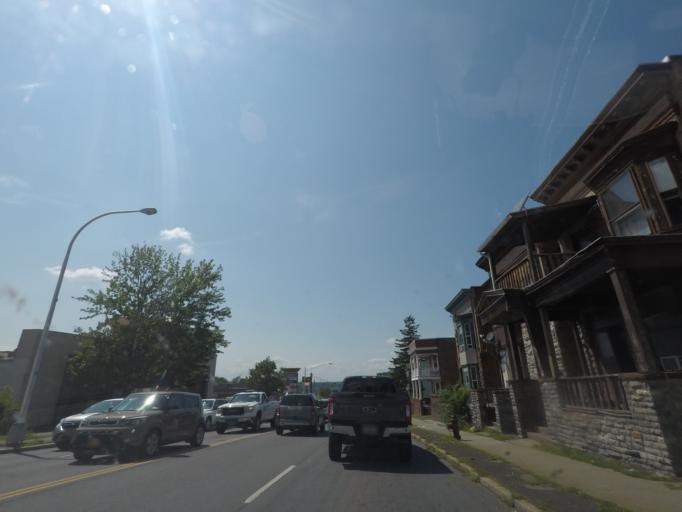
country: US
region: New York
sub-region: Albany County
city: Green Island
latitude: 42.7390
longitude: -73.6755
